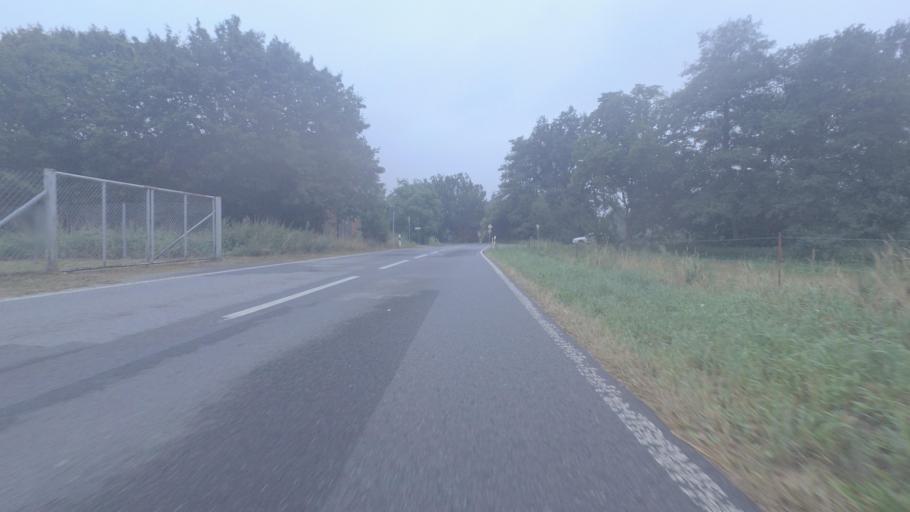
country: DE
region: Brandenburg
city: Heiligengrabe
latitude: 53.1449
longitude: 12.3427
